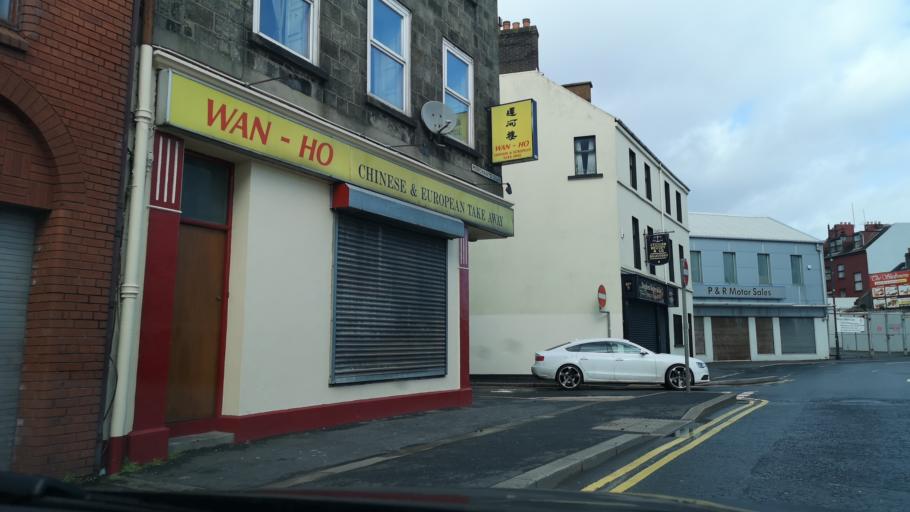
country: GB
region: Northern Ireland
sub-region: Newry and Mourne District
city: Newry
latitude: 54.1781
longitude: -6.3387
